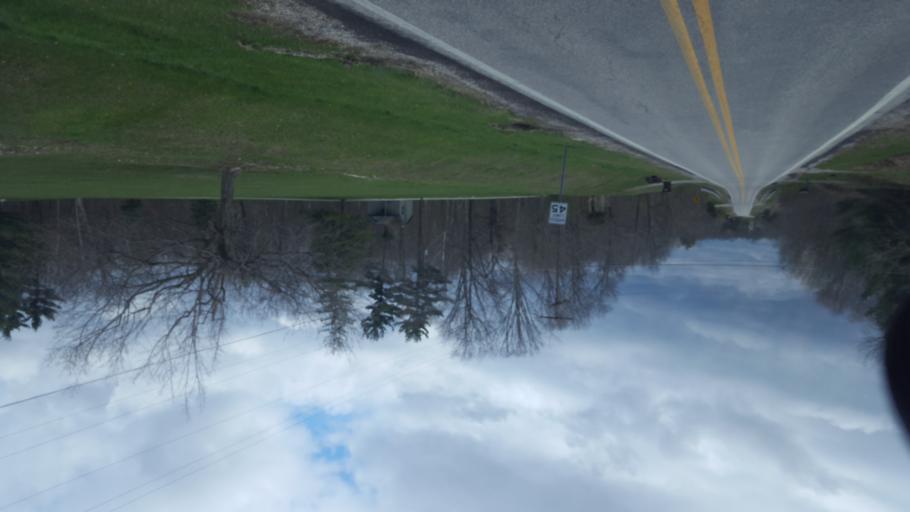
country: US
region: Ohio
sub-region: Franklin County
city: Westerville
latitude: 40.1530
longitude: -82.8566
